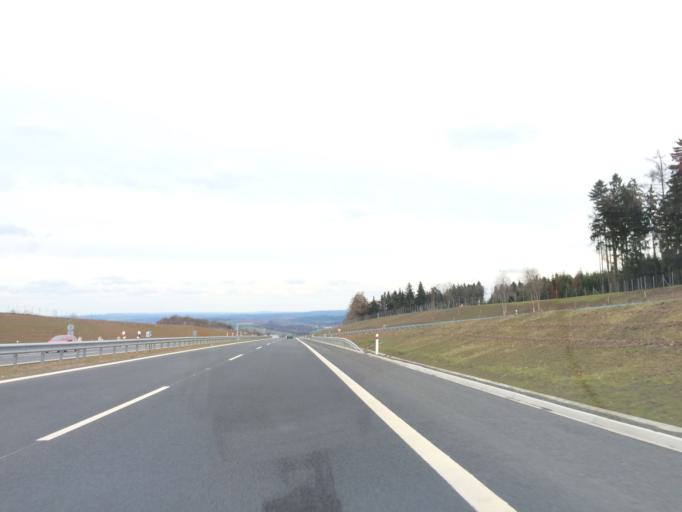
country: CZ
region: Ustecky
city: Lubenec
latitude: 50.1345
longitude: 13.2378
